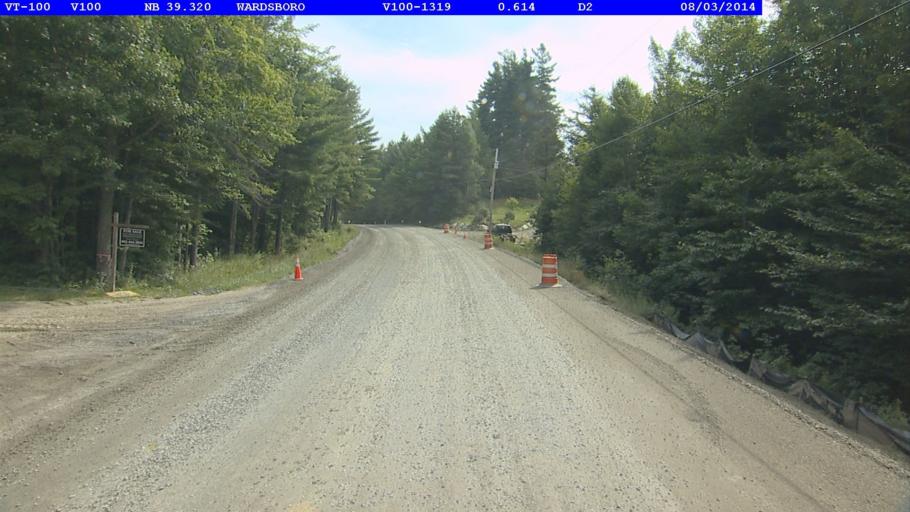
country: US
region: Vermont
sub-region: Windham County
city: Dover
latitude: 43.0108
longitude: -72.8670
